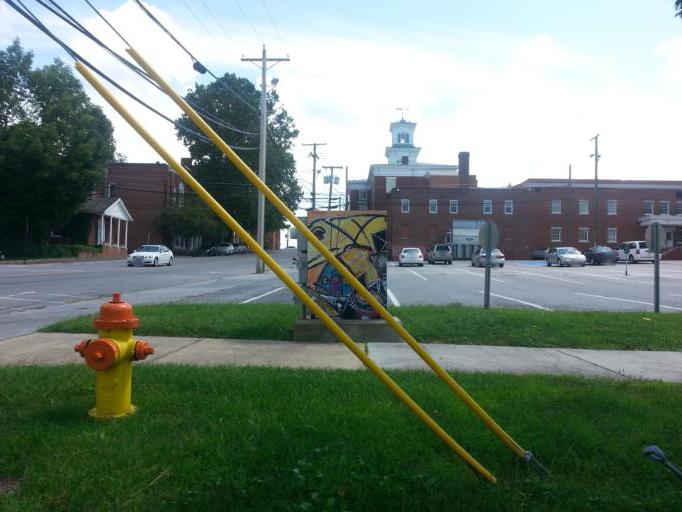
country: US
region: Virginia
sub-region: Washington County
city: Abingdon
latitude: 36.7133
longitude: -81.9704
